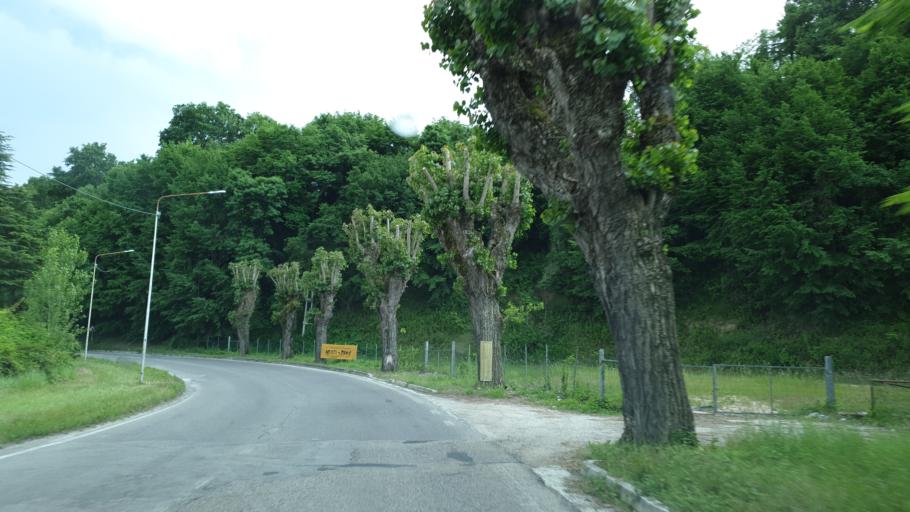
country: IT
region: Emilia-Romagna
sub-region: Provincia di Rimini
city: Talamello
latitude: 43.9049
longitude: 12.2933
